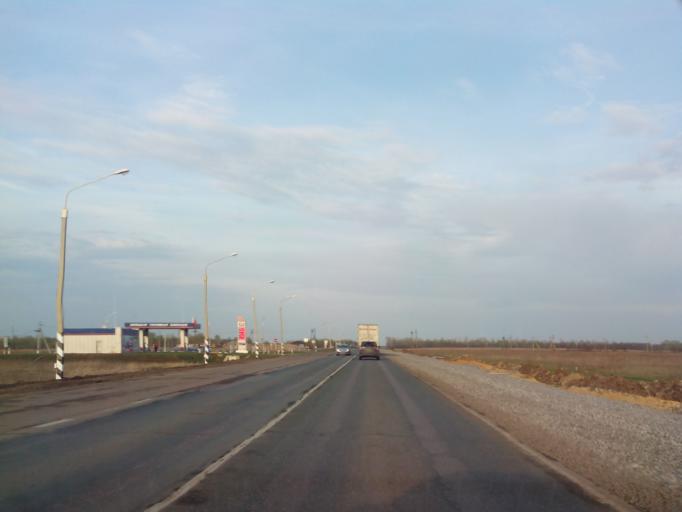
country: RU
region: Rjazan
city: Zarechnyy
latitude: 53.7522
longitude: 39.8148
